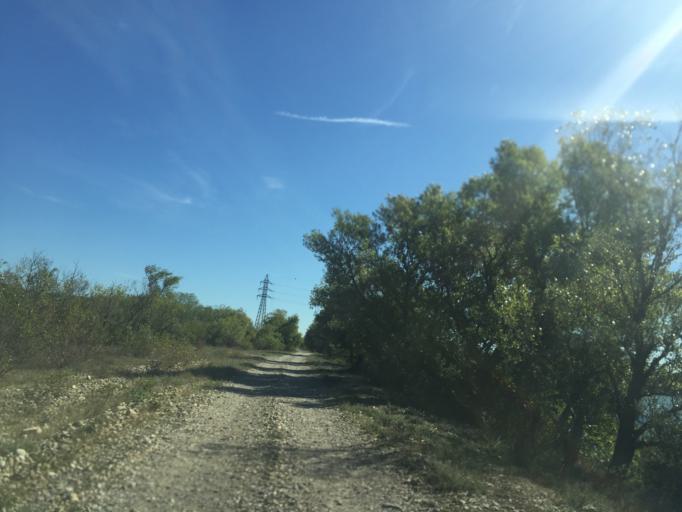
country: FR
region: Provence-Alpes-Cote d'Azur
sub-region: Departement du Vaucluse
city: Caderousse
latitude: 44.0890
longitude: 4.7385
